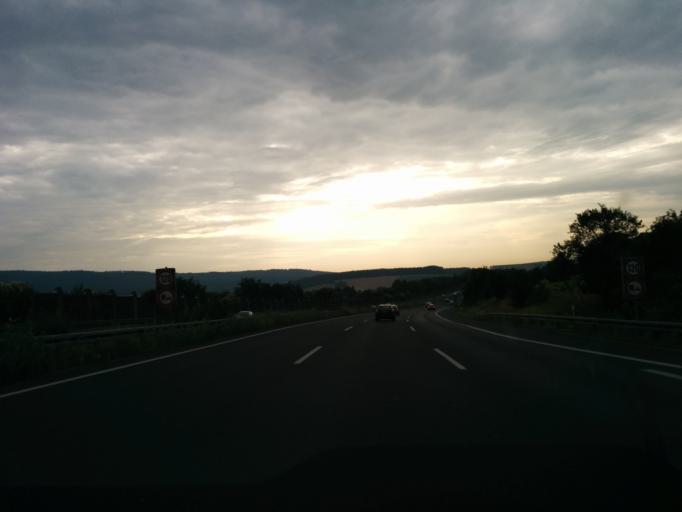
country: DE
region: Lower Saxony
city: Scheden
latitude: 51.3952
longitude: 9.7754
